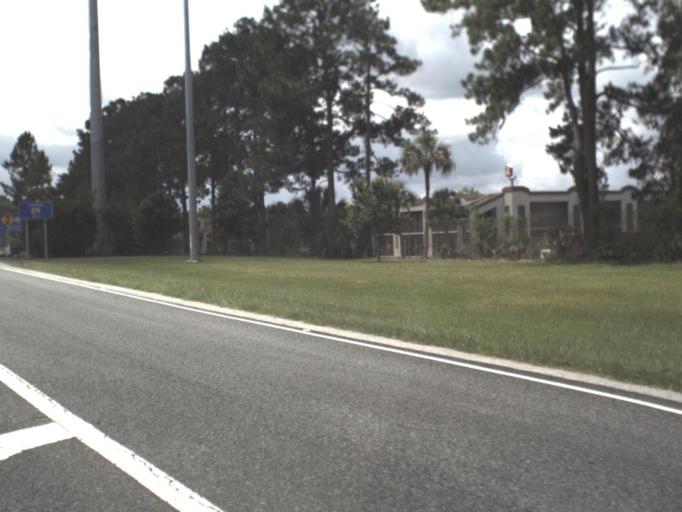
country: US
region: Florida
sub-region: Columbia County
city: Lake City
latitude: 30.1824
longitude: -82.6901
